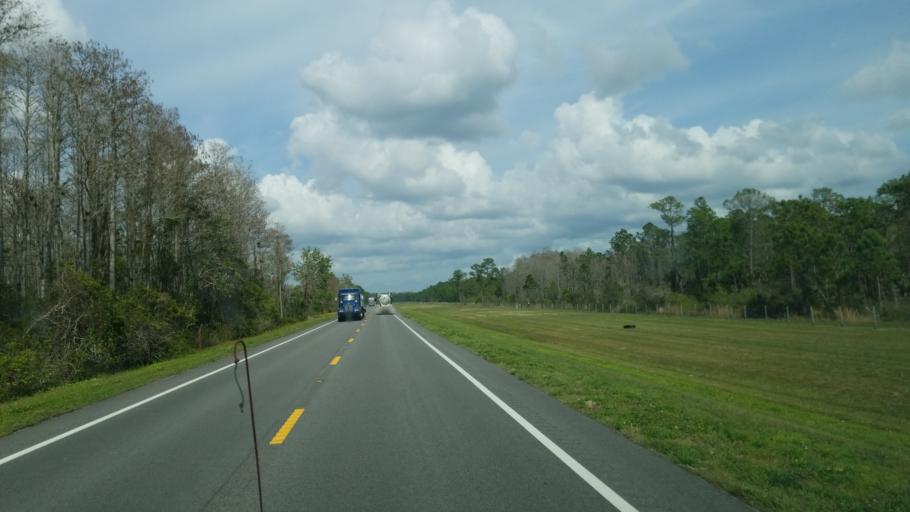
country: US
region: Florida
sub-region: Indian River County
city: Fellsmere
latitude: 27.7380
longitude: -80.9071
